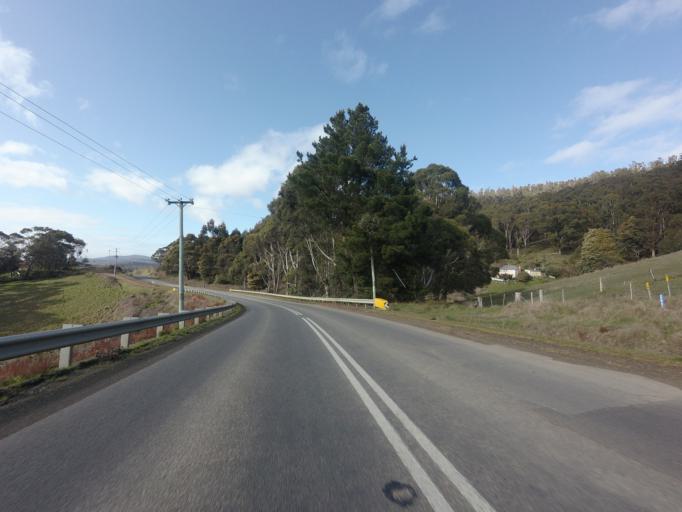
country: AU
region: Tasmania
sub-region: Huon Valley
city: Geeveston
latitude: -43.1813
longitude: 146.9517
